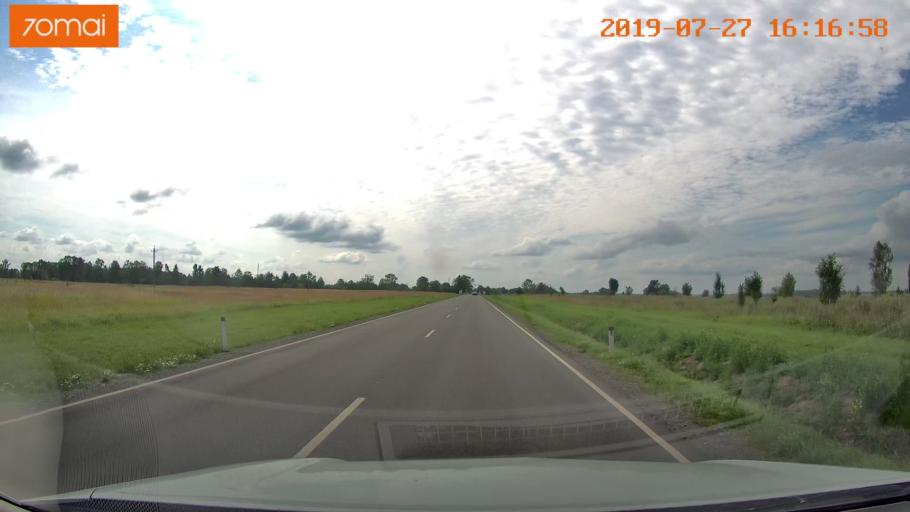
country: RU
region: Kaliningrad
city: Chernyakhovsk
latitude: 54.6237
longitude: 21.5601
